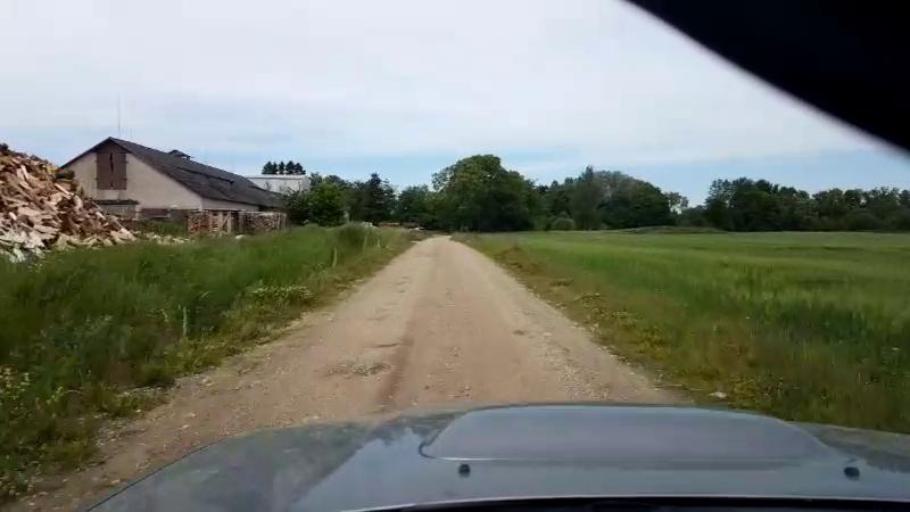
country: EE
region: Paernumaa
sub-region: Tootsi vald
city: Tootsi
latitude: 58.5364
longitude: 24.7338
